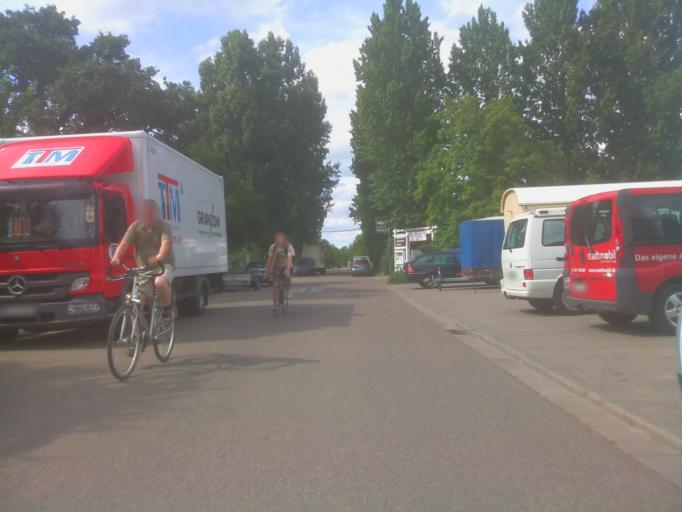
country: DE
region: Baden-Wuerttemberg
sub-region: Karlsruhe Region
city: Dossenheim
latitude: 49.4374
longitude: 8.6777
